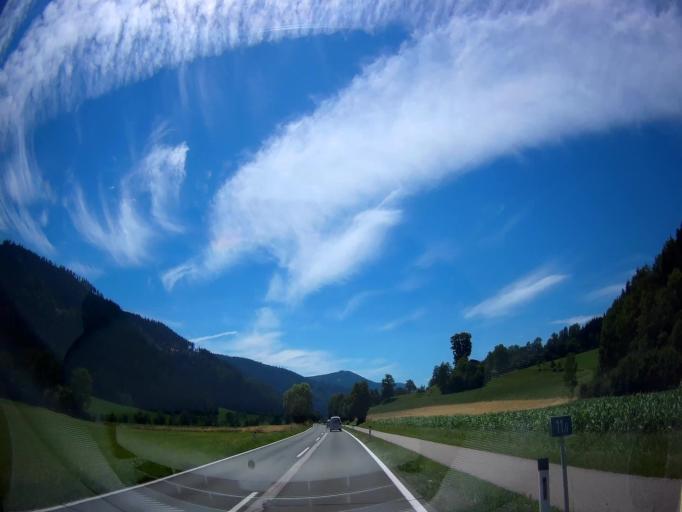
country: AT
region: Carinthia
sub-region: Politischer Bezirk Sankt Veit an der Glan
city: Strassburg
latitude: 46.8873
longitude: 14.3152
